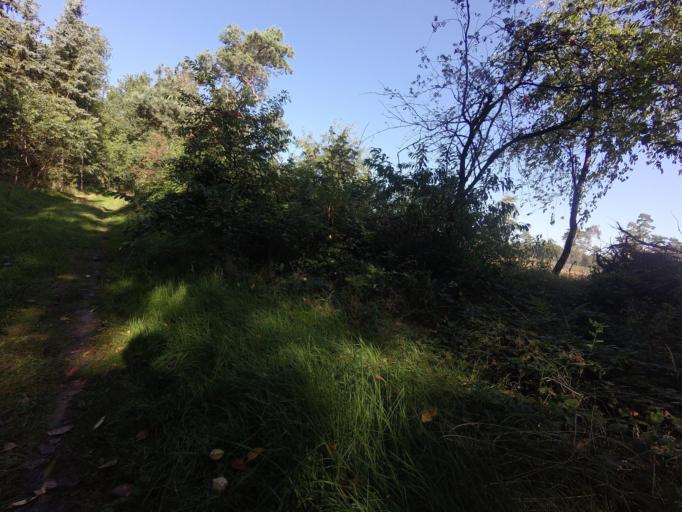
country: DE
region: Lower Saxony
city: Wielen
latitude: 52.5361
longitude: 6.7011
